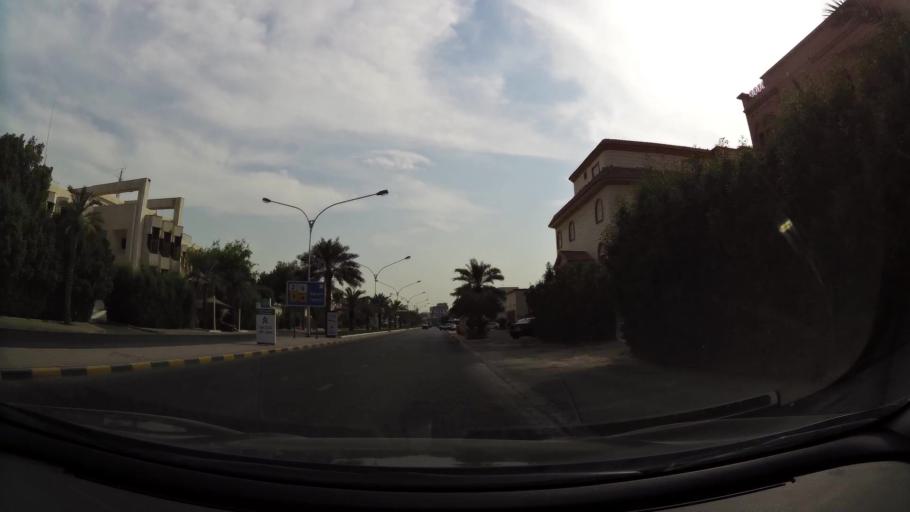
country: KW
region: Al Asimah
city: Ash Shamiyah
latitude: 29.3172
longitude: 47.9680
